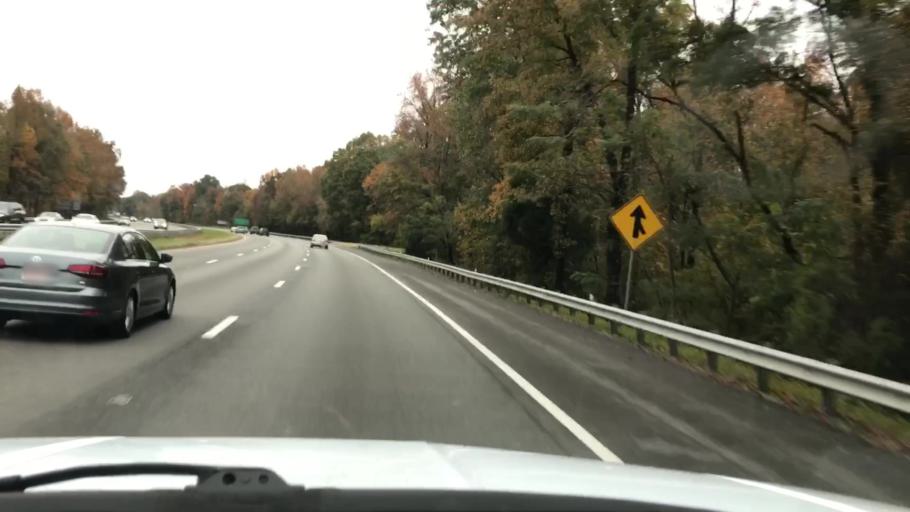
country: US
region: Virginia
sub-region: Henrico County
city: Chamberlayne
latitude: 37.6192
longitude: -77.4438
